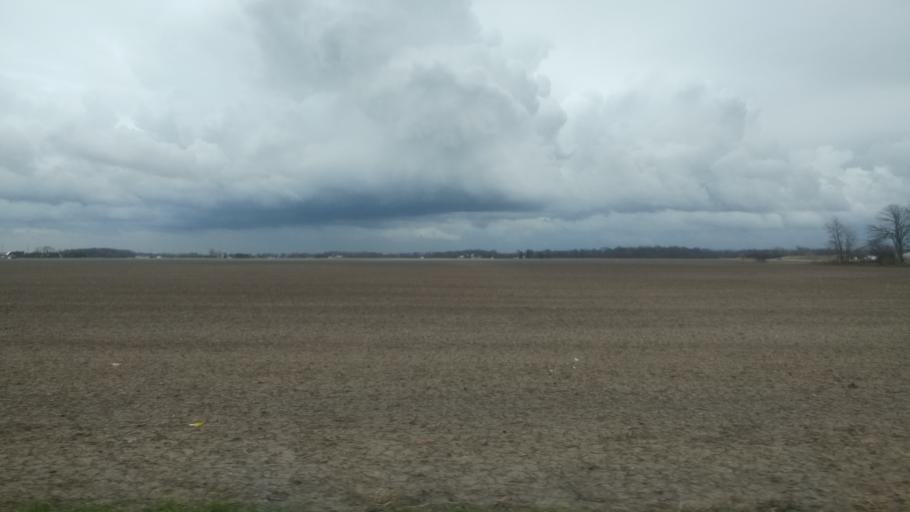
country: US
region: Ohio
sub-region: Wood County
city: Bowling Green
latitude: 41.3679
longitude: -83.6103
